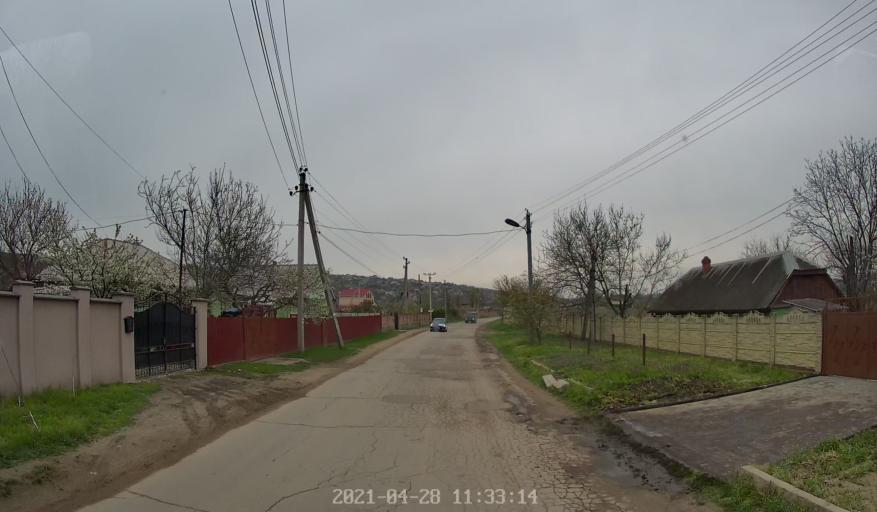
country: MD
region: Chisinau
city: Singera
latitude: 46.9628
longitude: 28.9369
